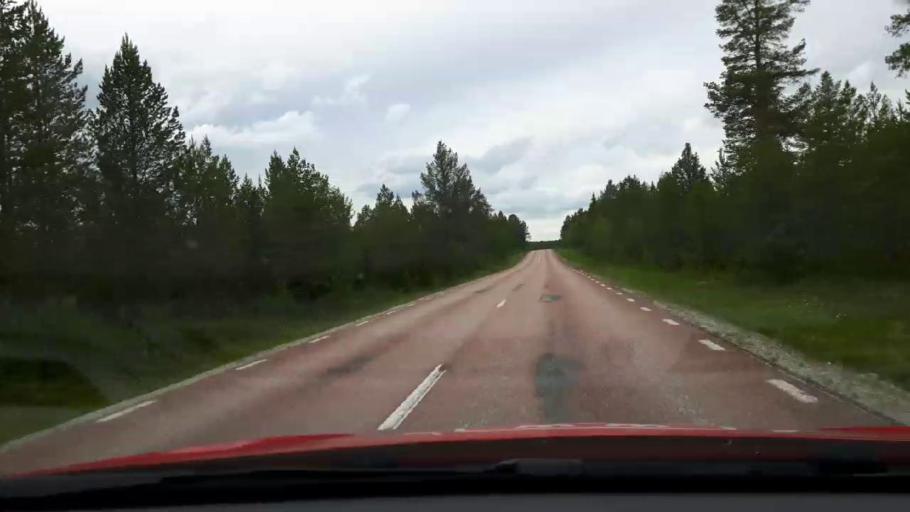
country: NO
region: Hedmark
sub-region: Engerdal
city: Engerdal
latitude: 62.4851
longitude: 12.6546
